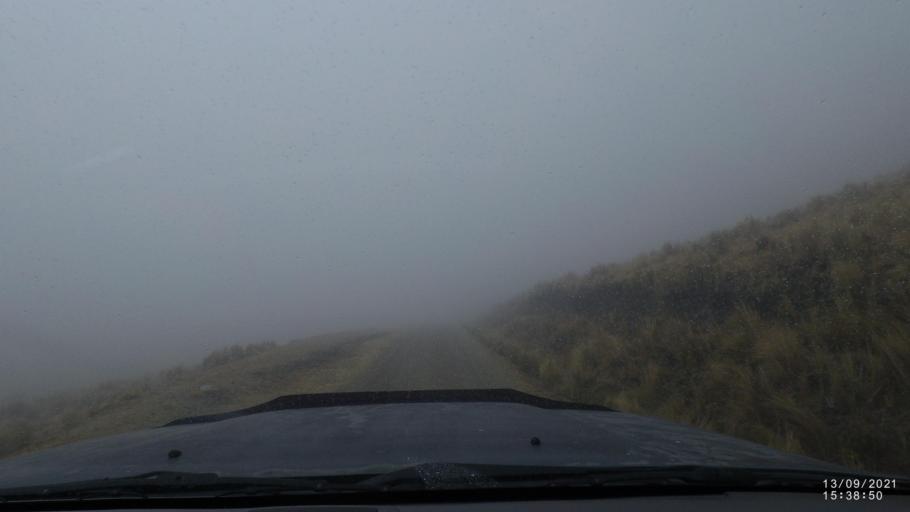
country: BO
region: Cochabamba
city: Colomi
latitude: -17.3269
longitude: -65.7213
